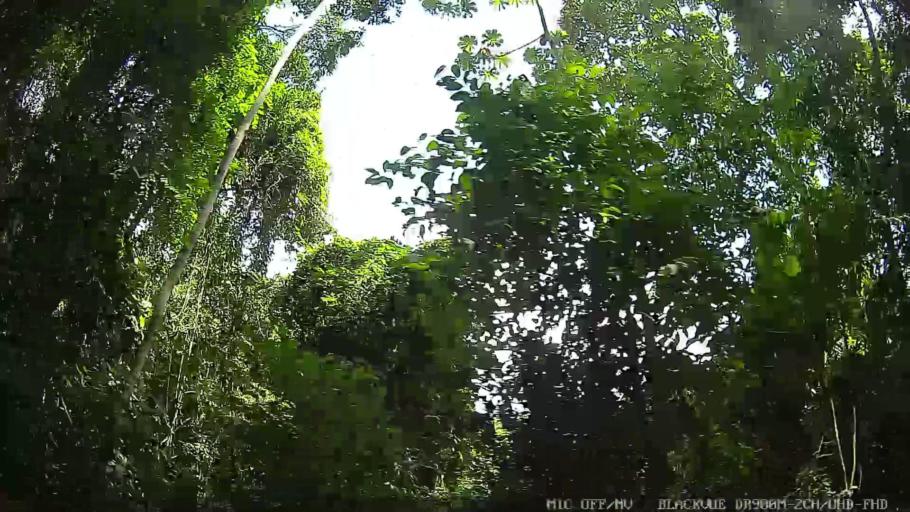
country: BR
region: Sao Paulo
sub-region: Caraguatatuba
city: Caraguatatuba
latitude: -23.6331
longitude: -45.4487
